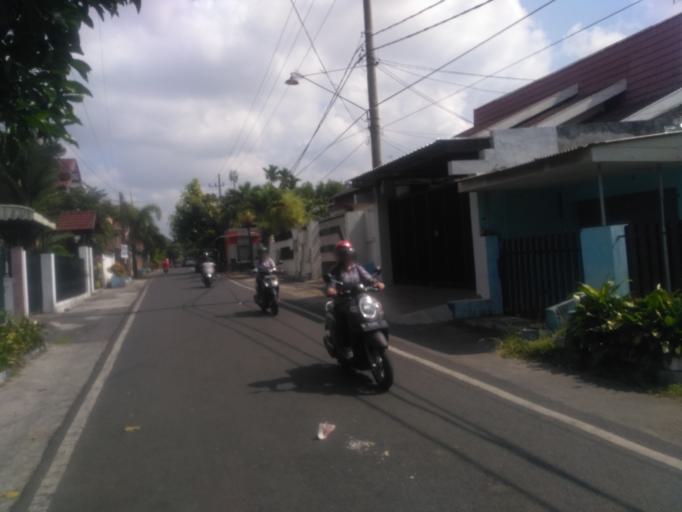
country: ID
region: East Java
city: Malang
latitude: -7.9434
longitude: 112.6368
